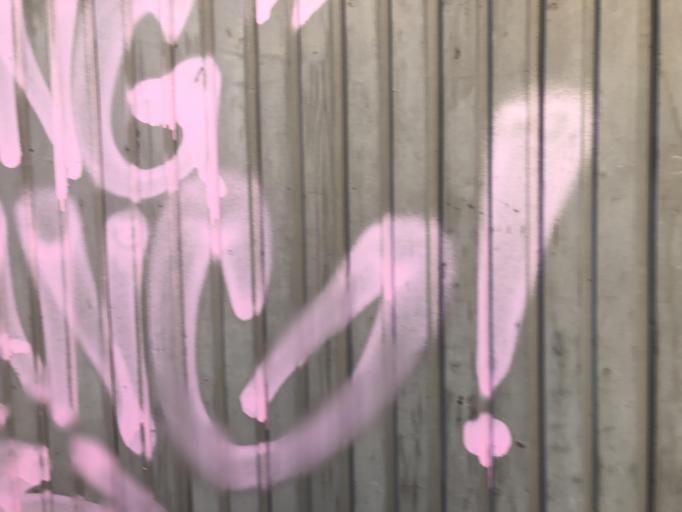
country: BJ
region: Borgou
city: Beterou
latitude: 9.4505
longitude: 2.0994
